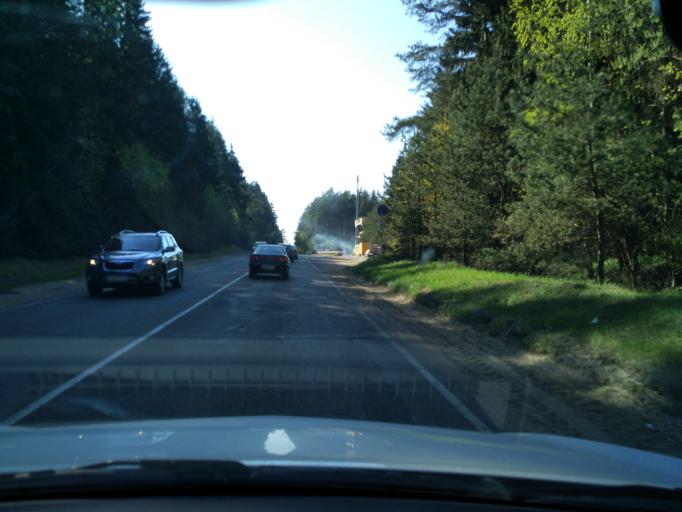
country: BY
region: Minsk
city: Borovlyany
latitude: 53.9620
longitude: 27.6859
